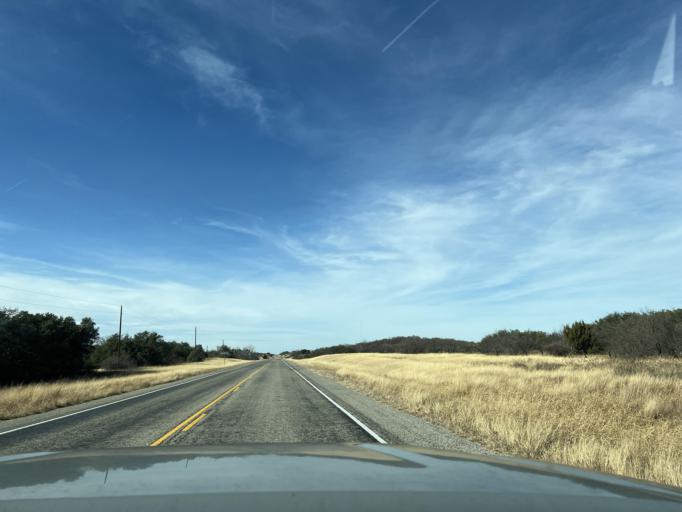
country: US
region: Texas
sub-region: Eastland County
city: Cisco
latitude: 32.4666
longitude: -99.0359
